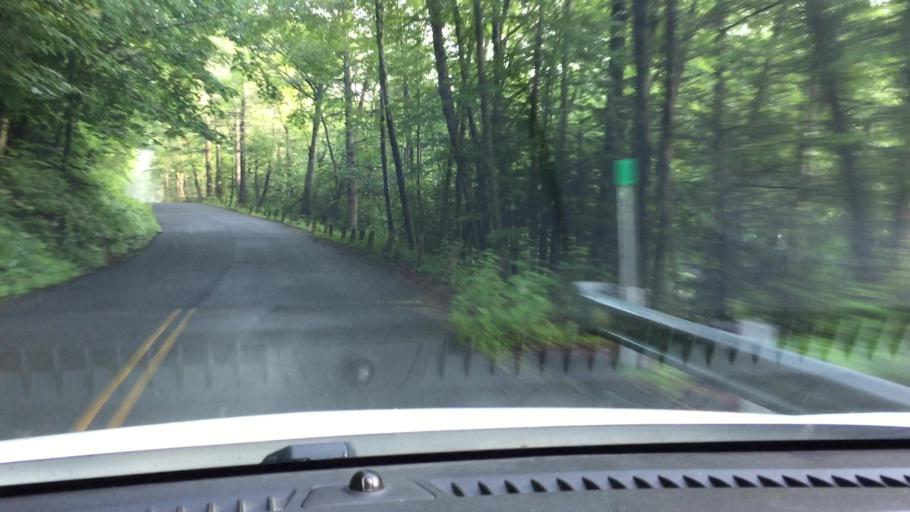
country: US
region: Massachusetts
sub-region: Hampshire County
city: Chesterfield
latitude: 42.3416
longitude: -72.9517
